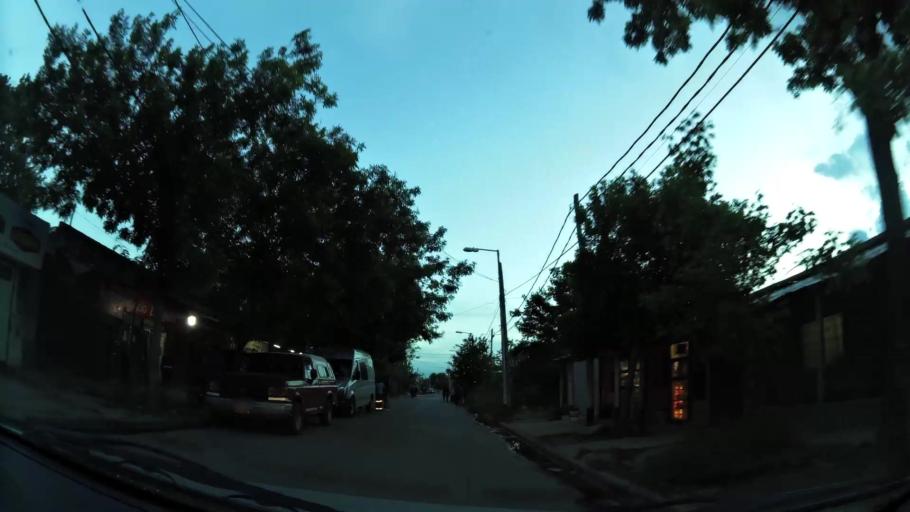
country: AR
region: Buenos Aires
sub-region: Partido de Avellaneda
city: Avellaneda
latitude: -34.6758
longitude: -58.3383
